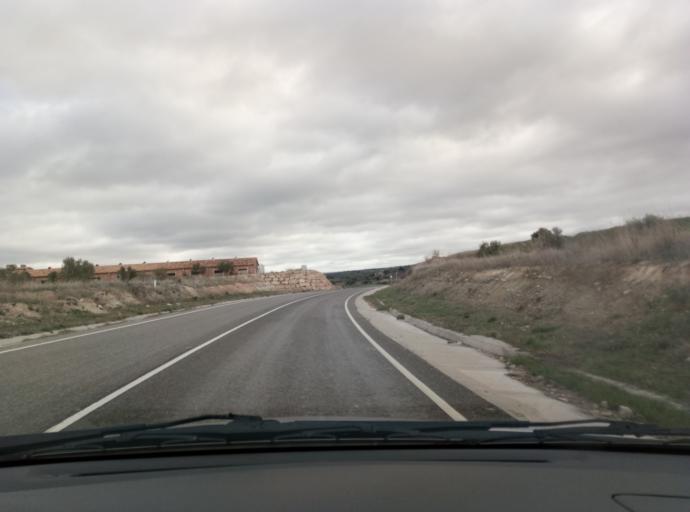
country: ES
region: Catalonia
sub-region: Provincia de Lleida
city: Vallbona de les Monges
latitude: 41.5637
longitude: 1.0634
